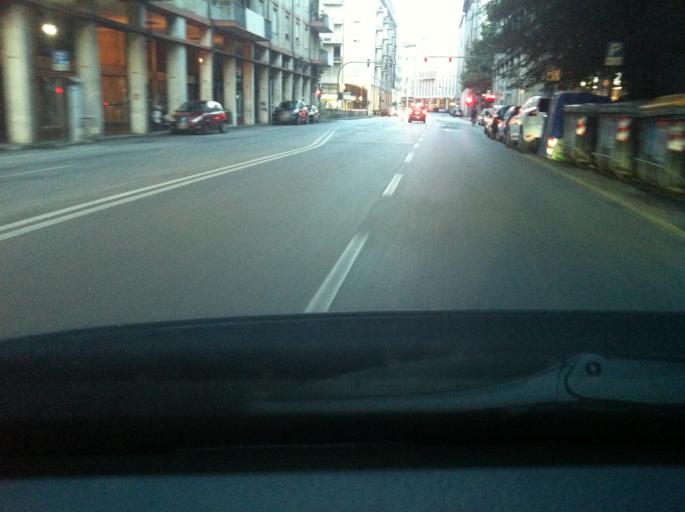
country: IT
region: Veneto
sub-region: Provincia di Padova
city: Padova
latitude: 45.4109
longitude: 11.8673
